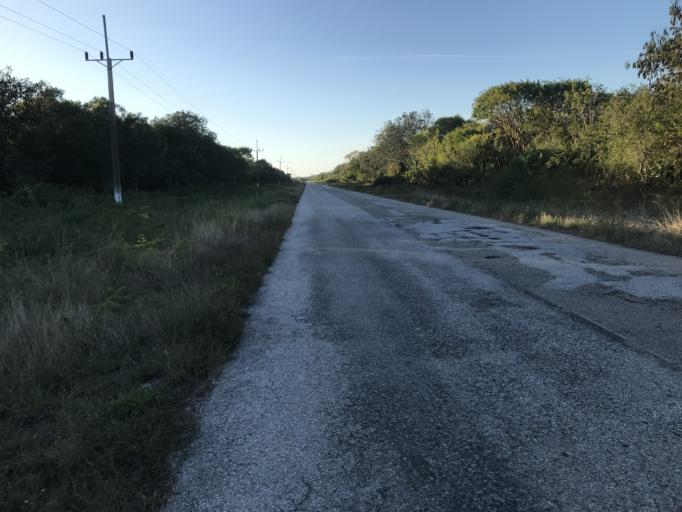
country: CU
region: Cienfuegos
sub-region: Municipio de Aguada de Pasajeros
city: Aguada de Pasajeros
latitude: 22.0773
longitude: -81.0652
